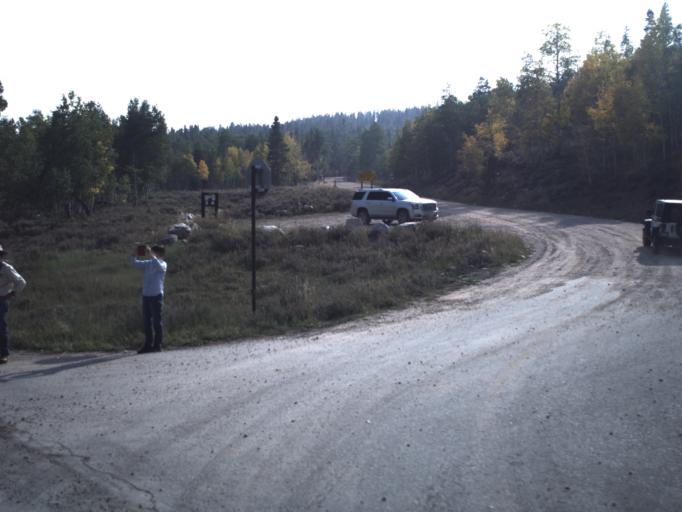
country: US
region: Wyoming
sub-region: Uinta County
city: Evanston
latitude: 40.8505
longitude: -110.8468
